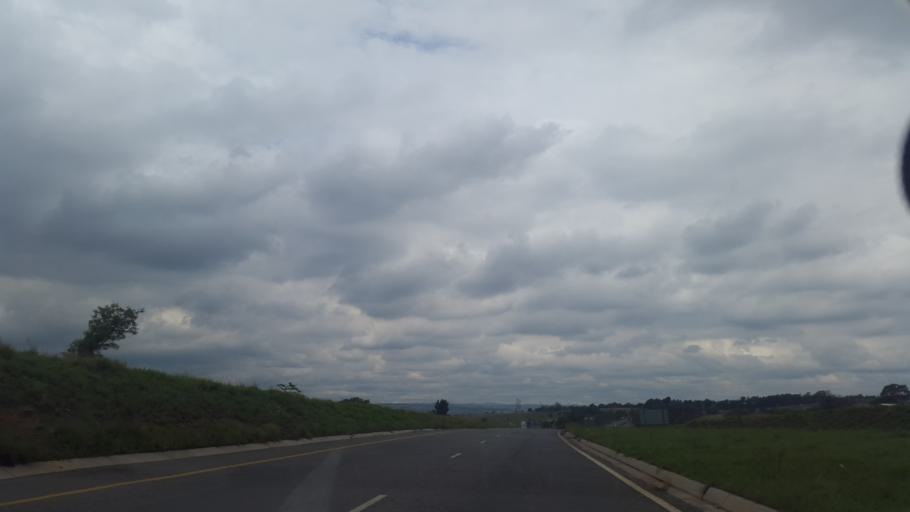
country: ZA
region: Gauteng
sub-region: City of Johannesburg Metropolitan Municipality
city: Diepsloot
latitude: -25.9673
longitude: 27.9265
